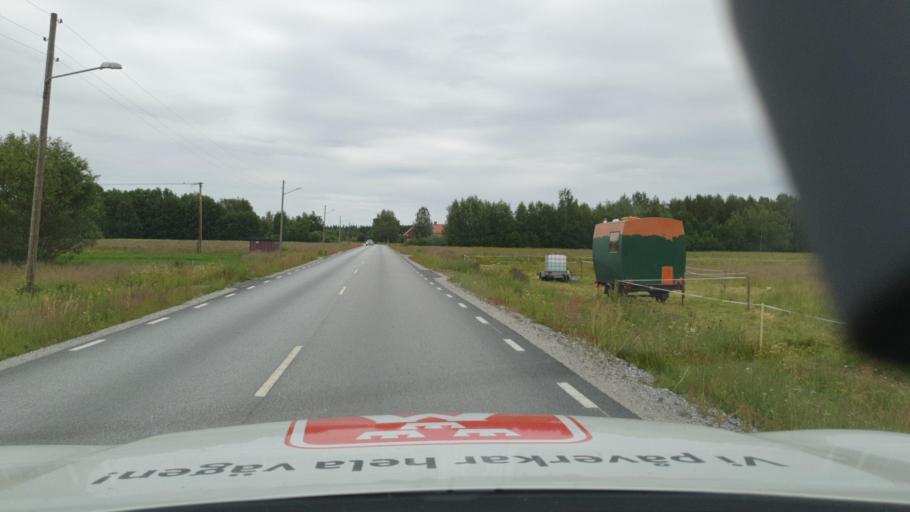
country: SE
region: Vaesterbotten
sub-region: Nordmalings Kommun
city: Nordmaling
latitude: 63.5598
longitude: 19.4075
